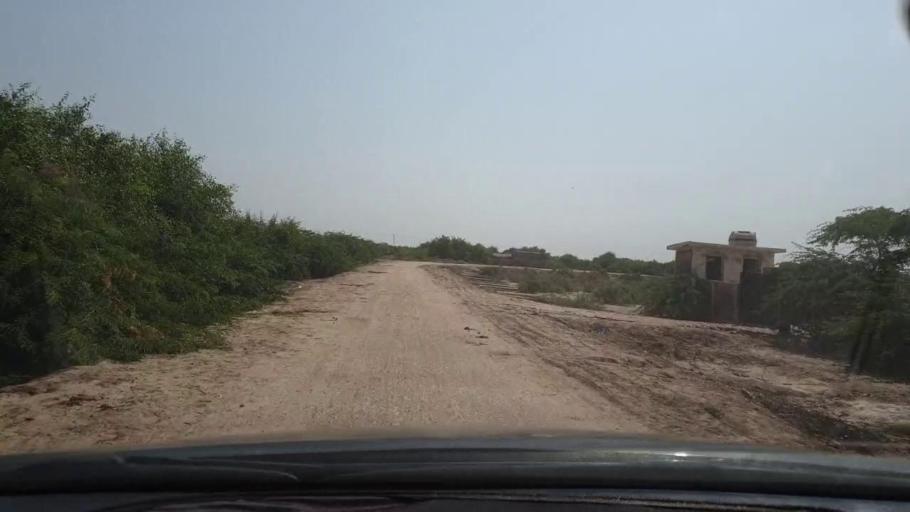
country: PK
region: Sindh
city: Naukot
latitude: 24.8069
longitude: 69.2441
